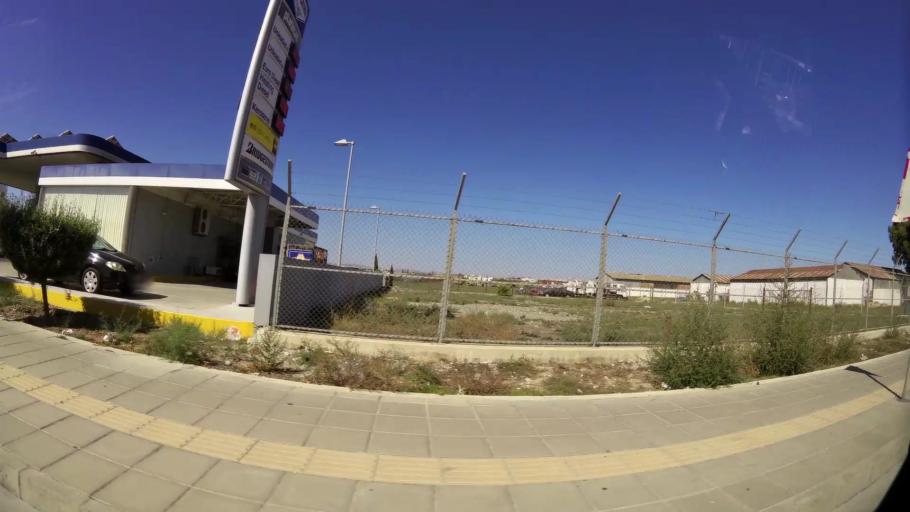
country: CY
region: Larnaka
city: Livadia
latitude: 34.9418
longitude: 33.6424
